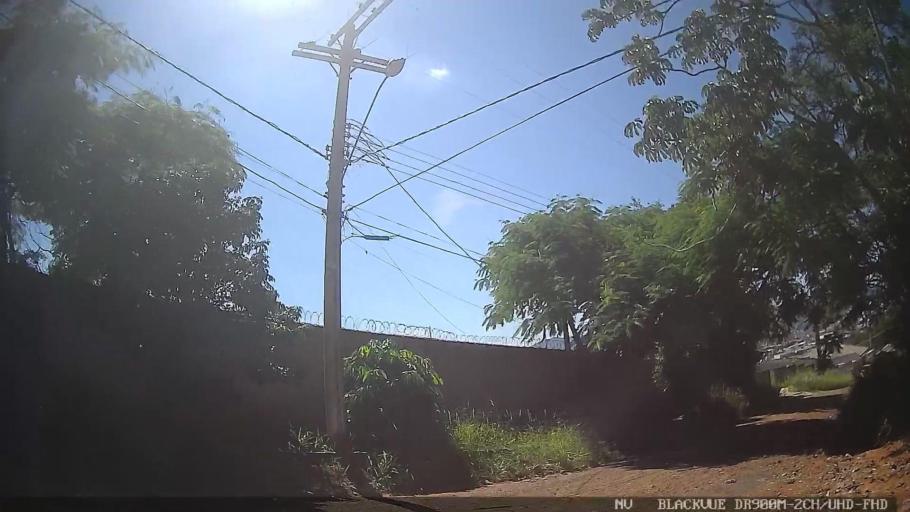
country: BR
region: Sao Paulo
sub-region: Atibaia
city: Atibaia
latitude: -23.1030
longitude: -46.5701
